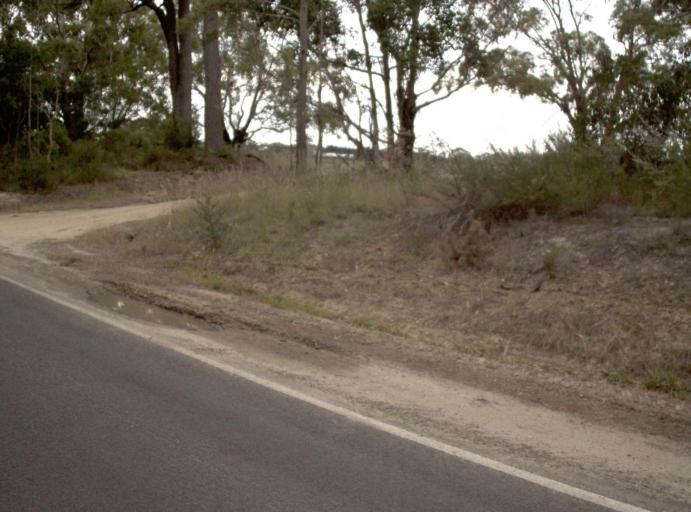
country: AU
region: Victoria
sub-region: Wellington
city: Sale
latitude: -38.5214
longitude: 146.8768
